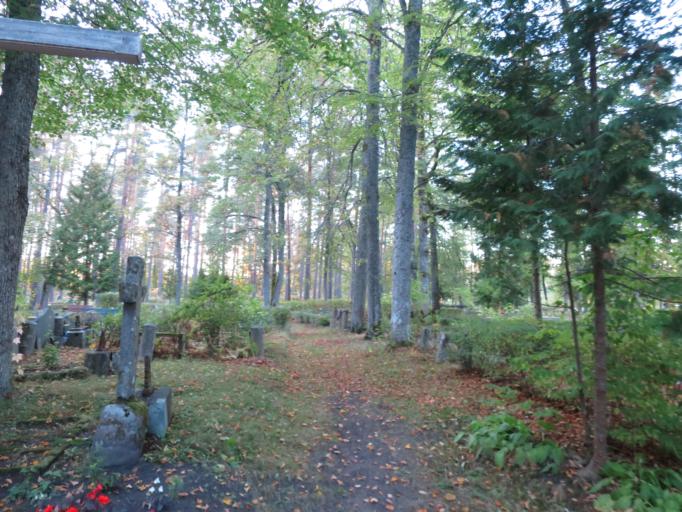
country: LV
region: Incukalns
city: Vangazi
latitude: 57.1267
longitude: 24.5631
